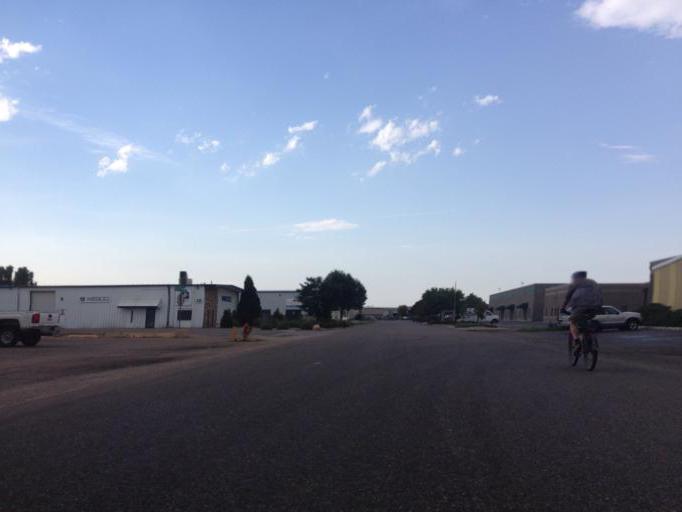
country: US
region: Colorado
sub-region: Larimer County
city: Fort Collins
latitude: 40.5878
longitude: -105.0468
